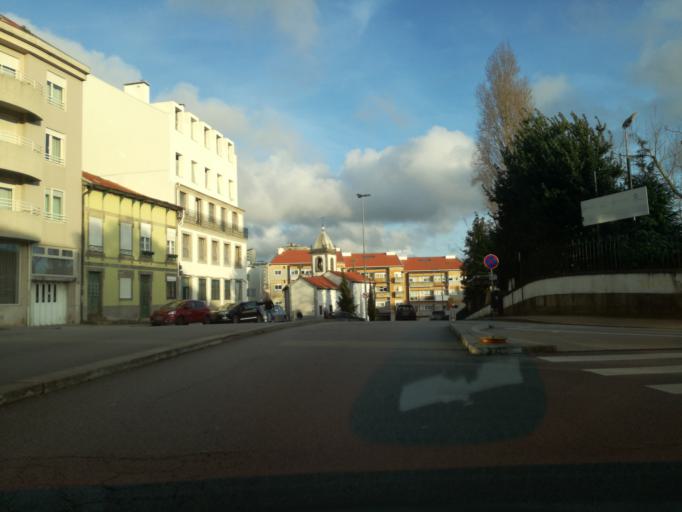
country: PT
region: Porto
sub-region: Porto
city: Porto
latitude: 41.1604
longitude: -8.6225
